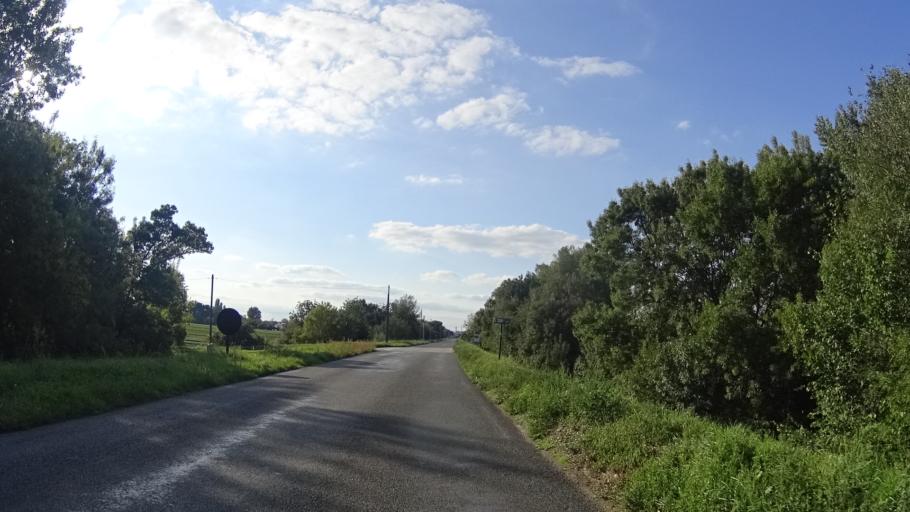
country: FR
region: Pays de la Loire
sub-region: Departement de Maine-et-Loire
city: Ingrandes
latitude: 47.3966
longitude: -0.8938
